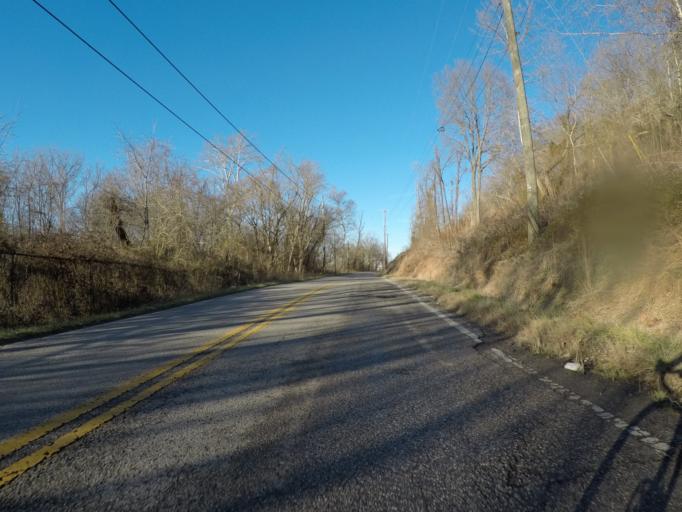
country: US
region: Kentucky
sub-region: Boyd County
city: Catlettsburg
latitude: 38.3959
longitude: -82.5932
